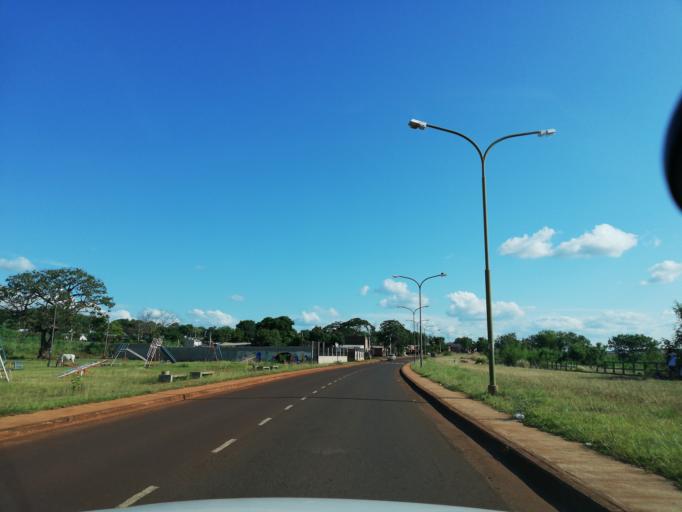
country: AR
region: Misiones
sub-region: Departamento de Capital
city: Posadas
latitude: -27.3772
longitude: -55.9518
